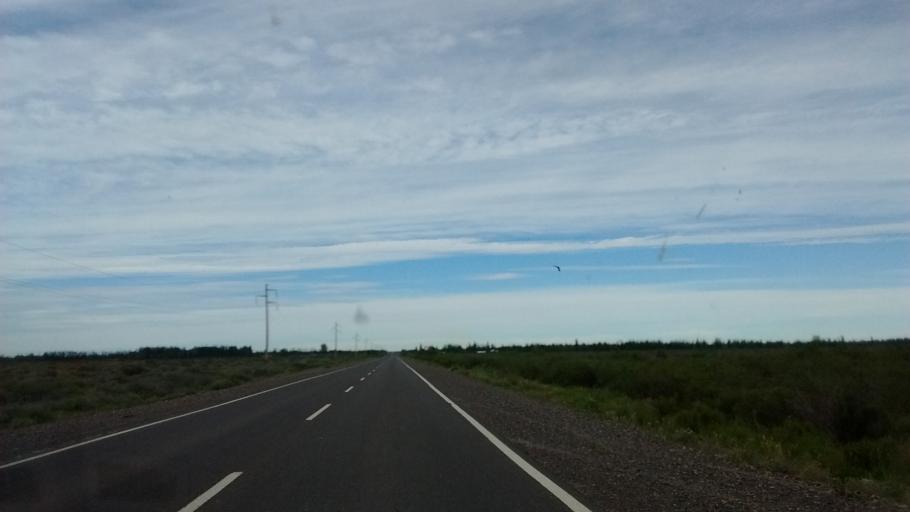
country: AR
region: Rio Negro
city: Contraalmirante Cordero
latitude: -38.6546
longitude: -68.1404
